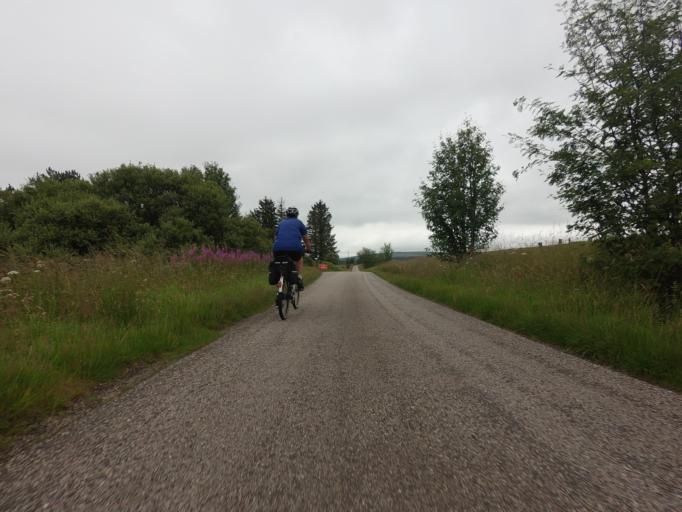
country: GB
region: Scotland
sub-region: Highland
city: Alness
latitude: 58.0097
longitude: -4.4031
